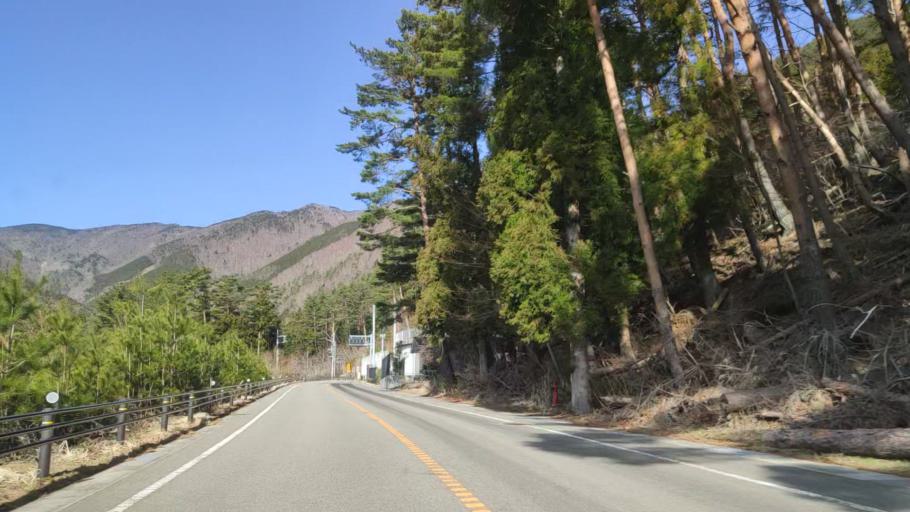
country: JP
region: Yamanashi
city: Fujikawaguchiko
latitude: 35.5278
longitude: 138.7172
